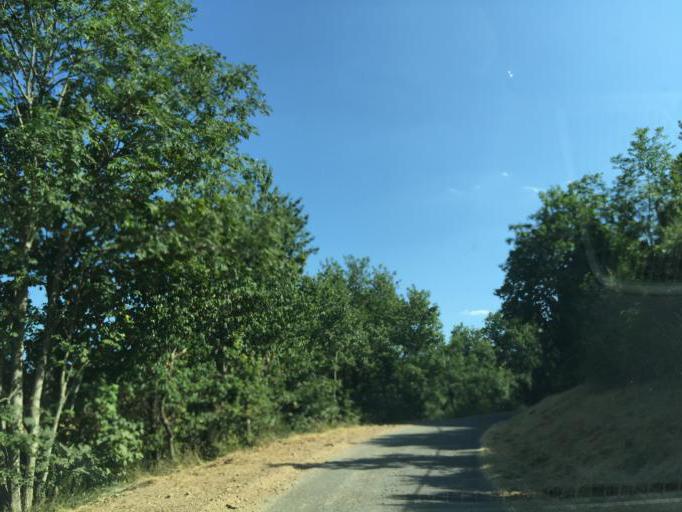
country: FR
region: Rhone-Alpes
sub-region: Departement de la Loire
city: Saint-Chamond
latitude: 45.4325
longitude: 4.4998
